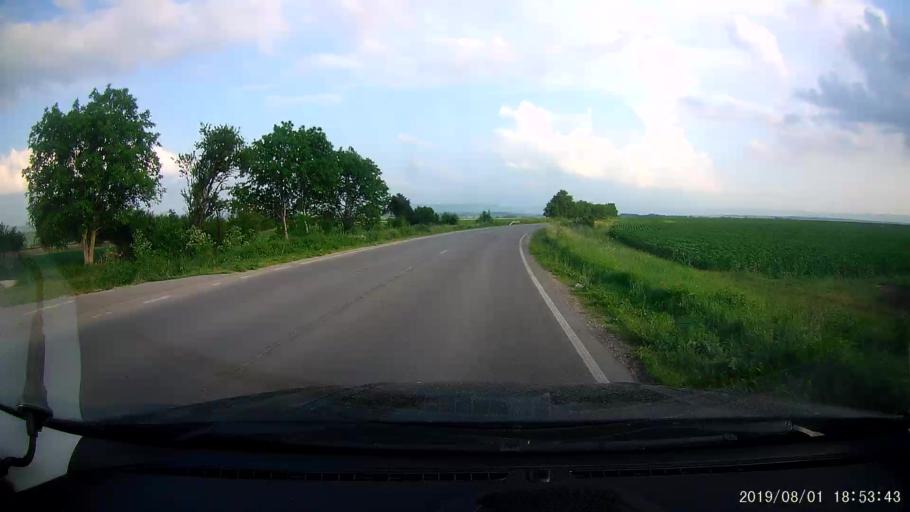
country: BG
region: Shumen
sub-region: Obshtina Shumen
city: Shumen
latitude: 43.2161
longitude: 26.9972
